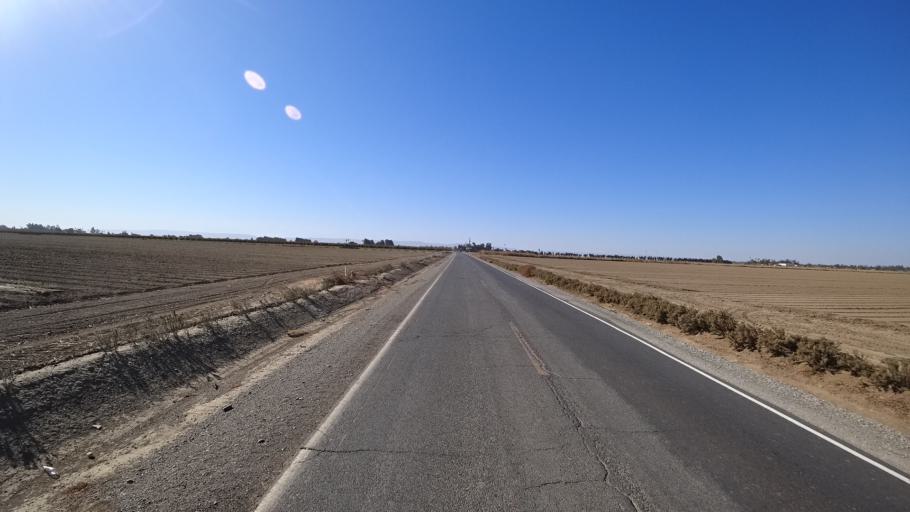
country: US
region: California
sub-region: Yolo County
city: Woodland
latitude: 38.6411
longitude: -121.7731
